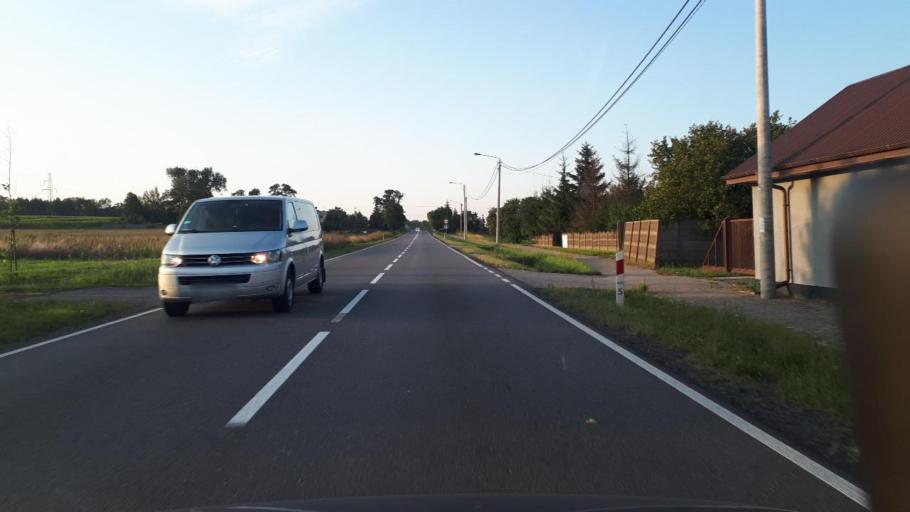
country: PL
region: Greater Poland Voivodeship
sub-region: Powiat ostrzeszowski
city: Ostrzeszow
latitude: 51.3566
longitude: 17.9469
